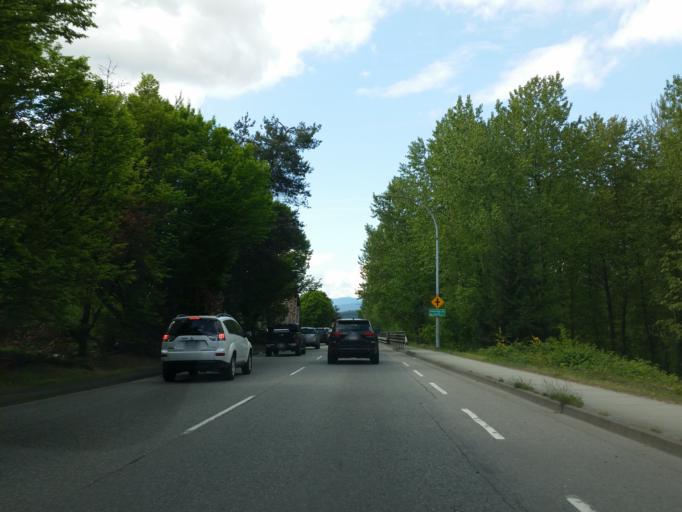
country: CA
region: British Columbia
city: Coquitlam
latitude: 49.2687
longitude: -122.7788
